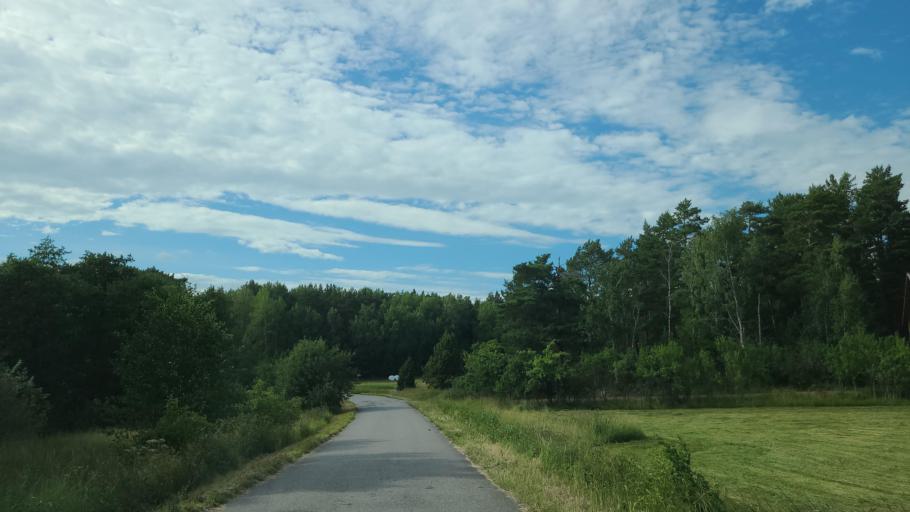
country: FI
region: Varsinais-Suomi
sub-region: Turku
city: Rymaettylae
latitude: 60.2867
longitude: 21.9698
